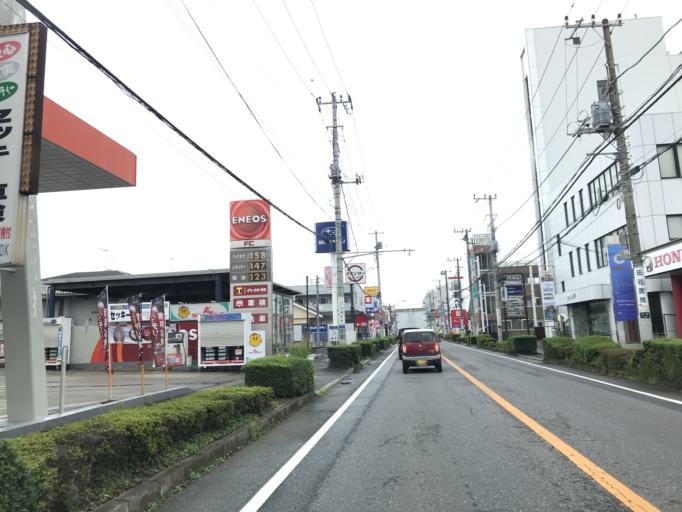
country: JP
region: Ibaraki
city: Naka
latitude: 36.0800
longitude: 140.1915
